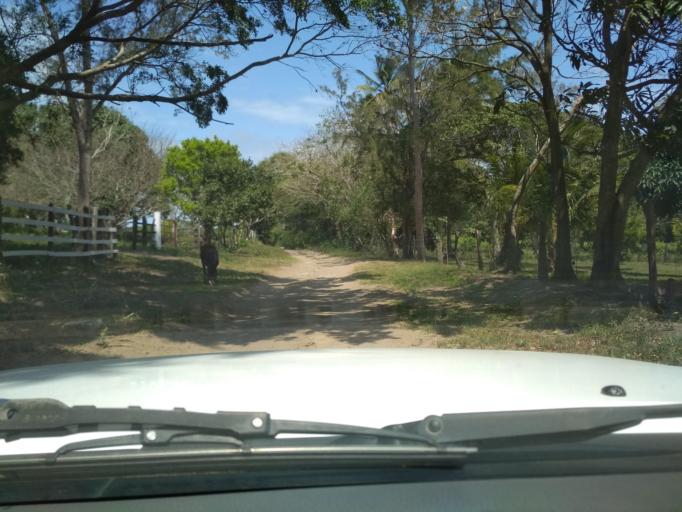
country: MX
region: Veracruz
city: Anton Lizardo
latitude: 19.0111
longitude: -95.9888
